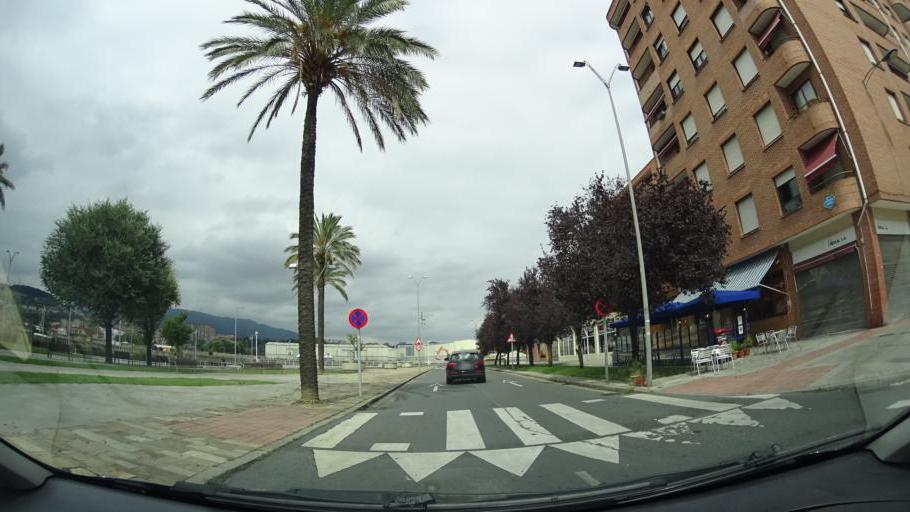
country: ES
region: Basque Country
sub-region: Bizkaia
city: Erandio
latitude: 43.2835
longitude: -2.9659
